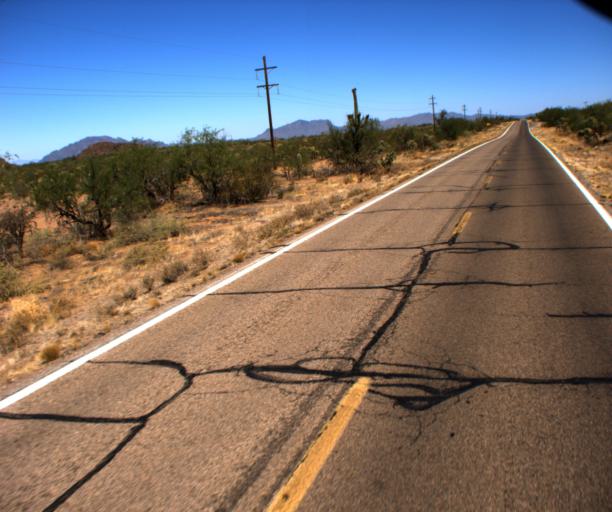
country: US
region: Arizona
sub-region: Pima County
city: Sells
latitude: 31.9644
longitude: -111.9538
